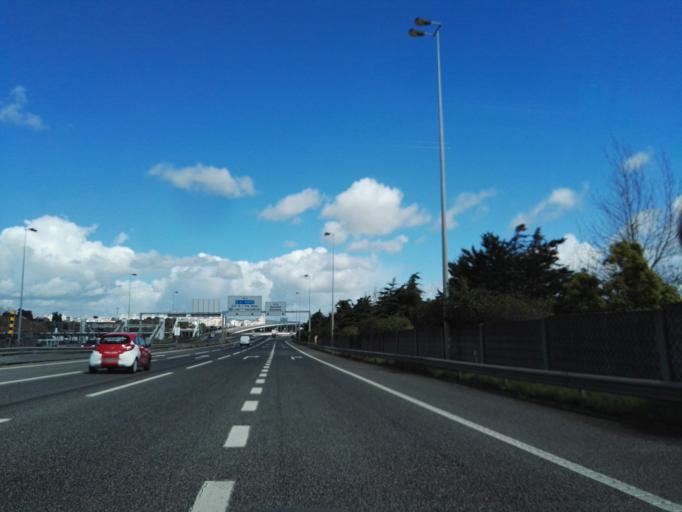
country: PT
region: Lisbon
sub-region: Loures
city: Sacavem
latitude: 38.7927
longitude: -9.0989
